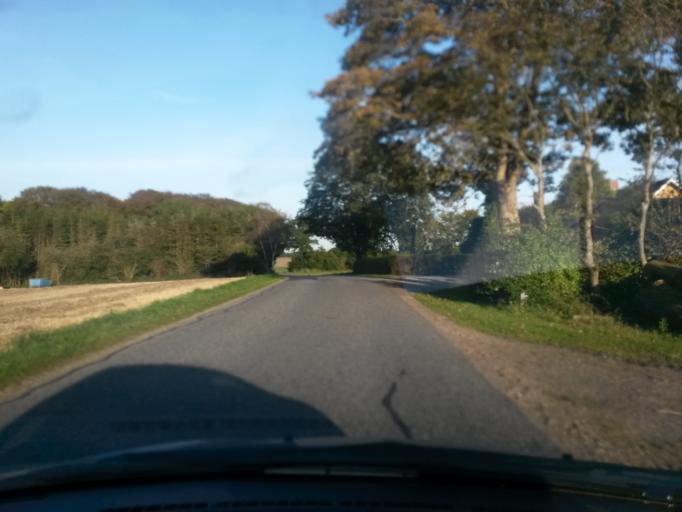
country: DK
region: Central Jutland
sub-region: Silkeborg Kommune
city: Kjellerup
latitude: 56.3173
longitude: 9.3953
